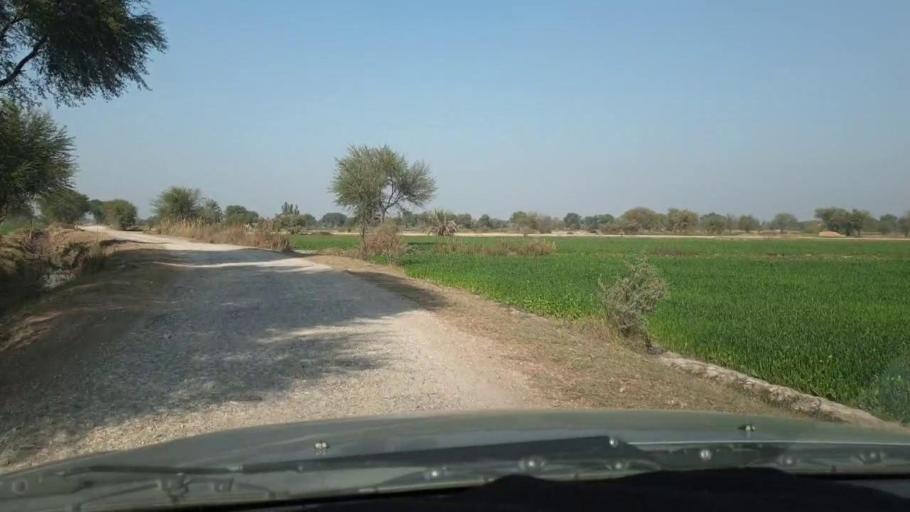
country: PK
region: Sindh
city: Mirpur Mathelo
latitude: 27.9309
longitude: 69.5633
